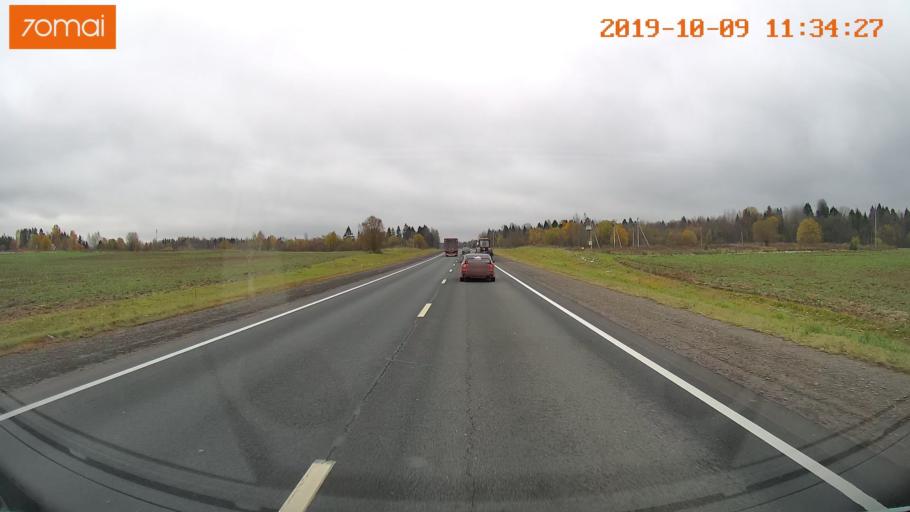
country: RU
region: Vologda
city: Gryazovets
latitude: 59.0159
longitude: 40.1187
